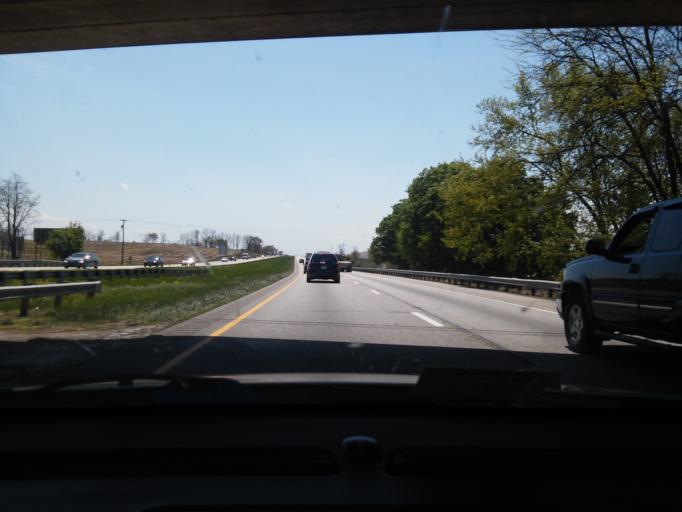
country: US
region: Pennsylvania
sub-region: Franklin County
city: Chambersburg
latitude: 39.8924
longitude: -77.6691
